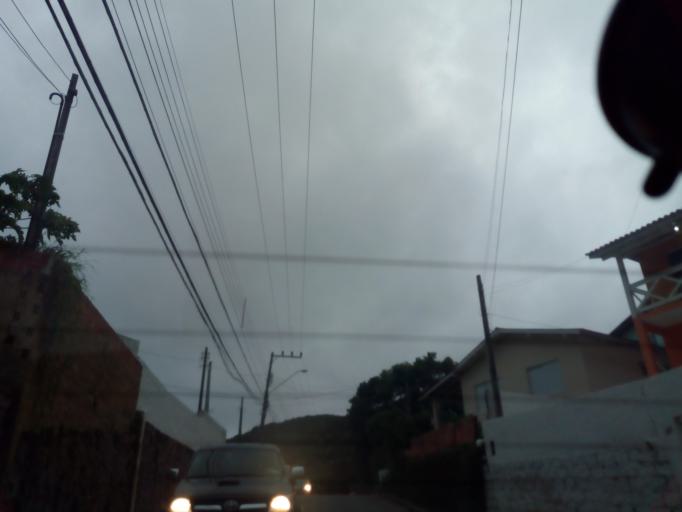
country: BR
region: Santa Catarina
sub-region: Florianopolis
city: Itacorubi
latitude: -27.3936
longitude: -48.4227
